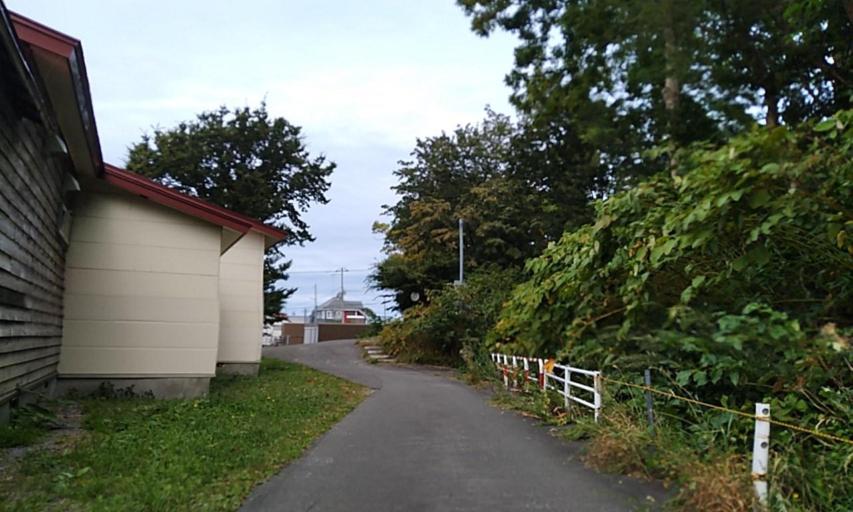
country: JP
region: Hokkaido
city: Rumoi
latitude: 43.8556
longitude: 141.5242
